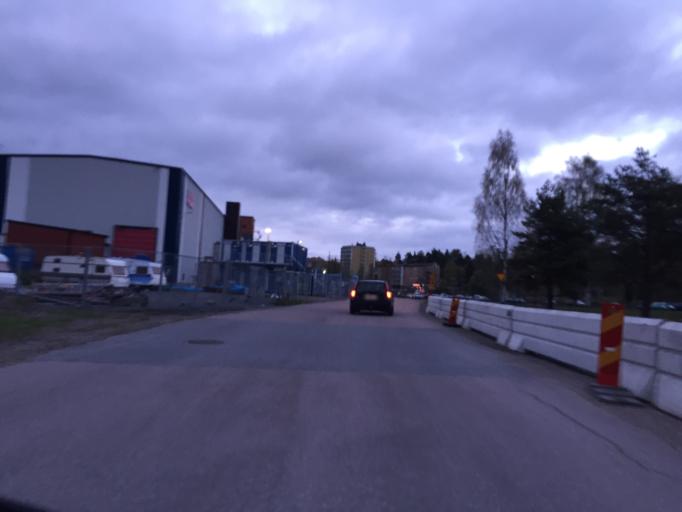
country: SE
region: Dalarna
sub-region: Ludvika Kommun
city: Ludvika
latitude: 60.1386
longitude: 15.1747
